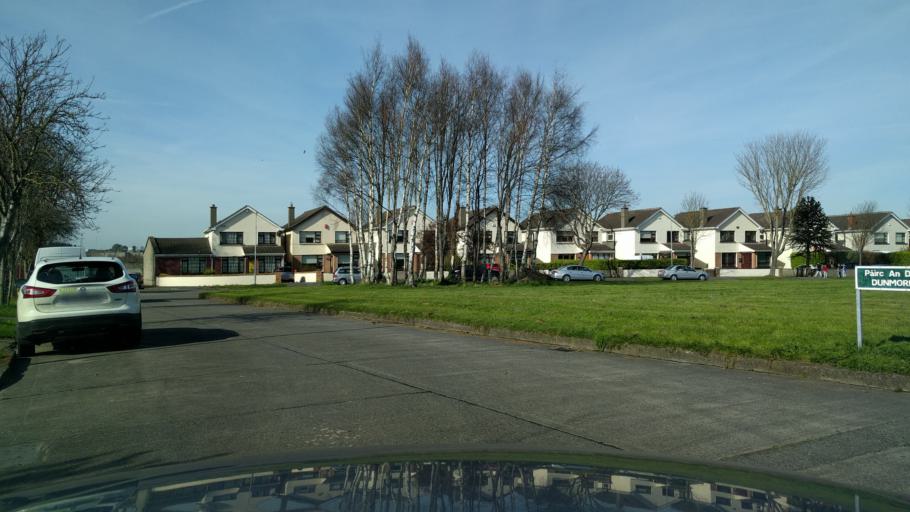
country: IE
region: Leinster
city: Tallaght
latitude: 53.3100
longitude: -6.3688
